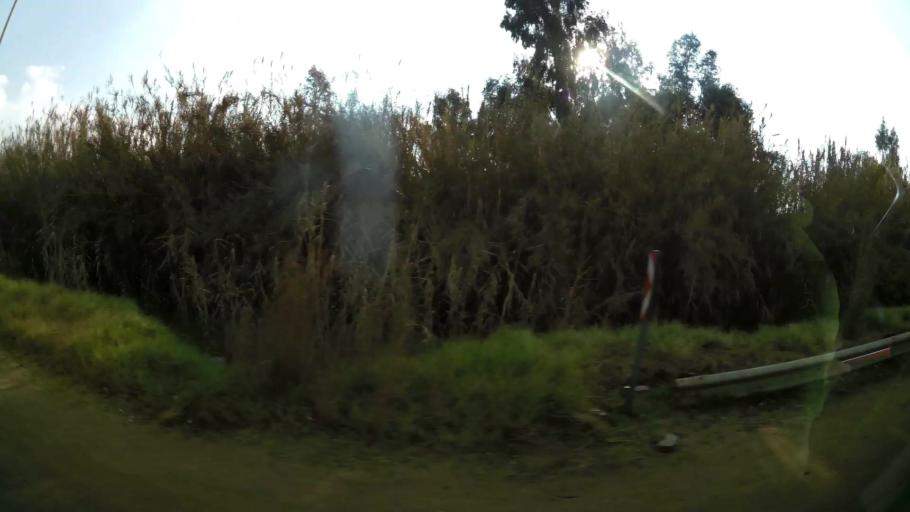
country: ZA
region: Gauteng
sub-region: Ekurhuleni Metropolitan Municipality
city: Tembisa
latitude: -26.0831
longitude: 28.2819
